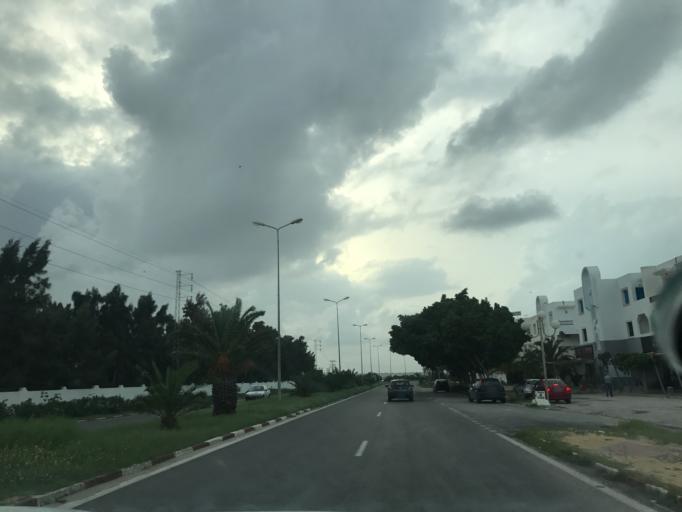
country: TN
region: Al Munastir
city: Sahline
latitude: 35.7575
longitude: 10.7360
